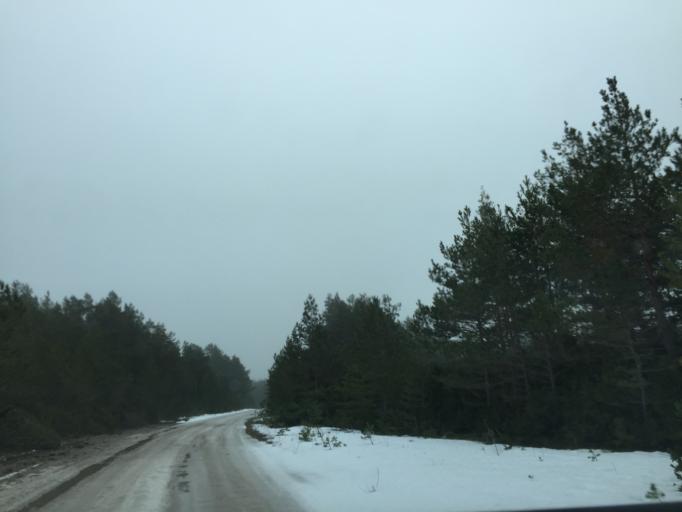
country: EE
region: Saare
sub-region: Kuressaare linn
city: Kuressaare
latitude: 58.5072
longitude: 21.9579
